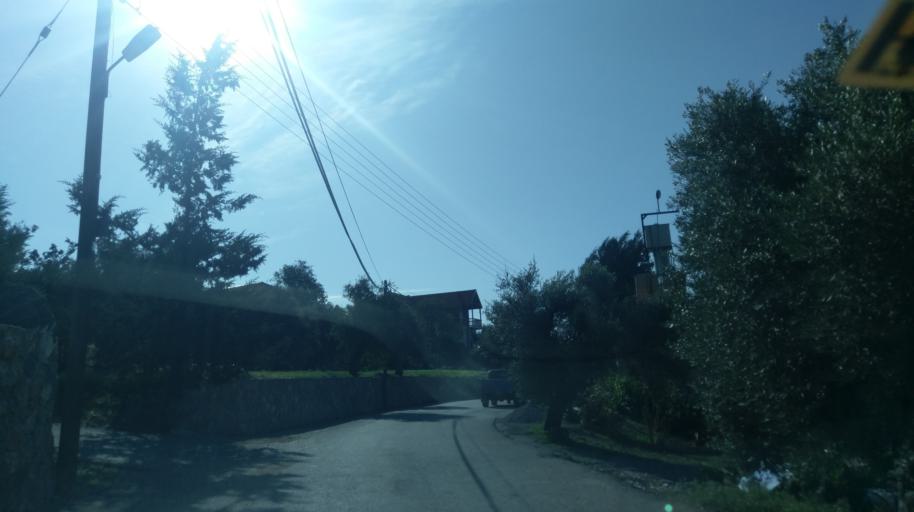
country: CY
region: Keryneia
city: Kyrenia
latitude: 35.2745
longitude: 33.3870
